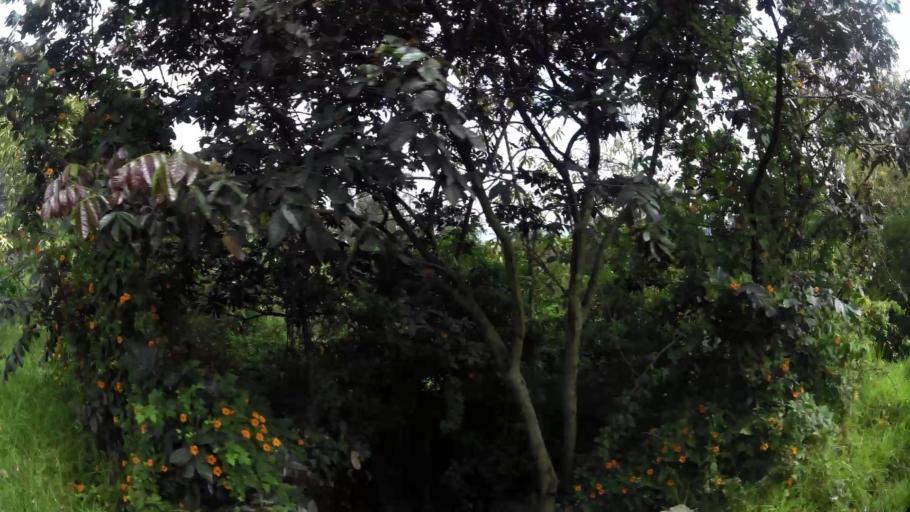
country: EC
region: Pichincha
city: Sangolqui
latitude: -0.3057
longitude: -78.4225
